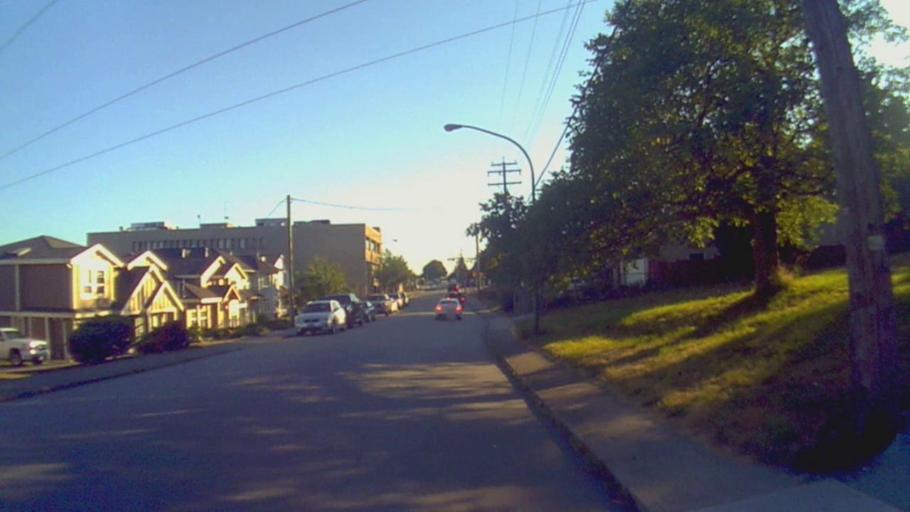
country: CA
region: British Columbia
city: New Westminster
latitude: 49.2212
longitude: -122.9282
